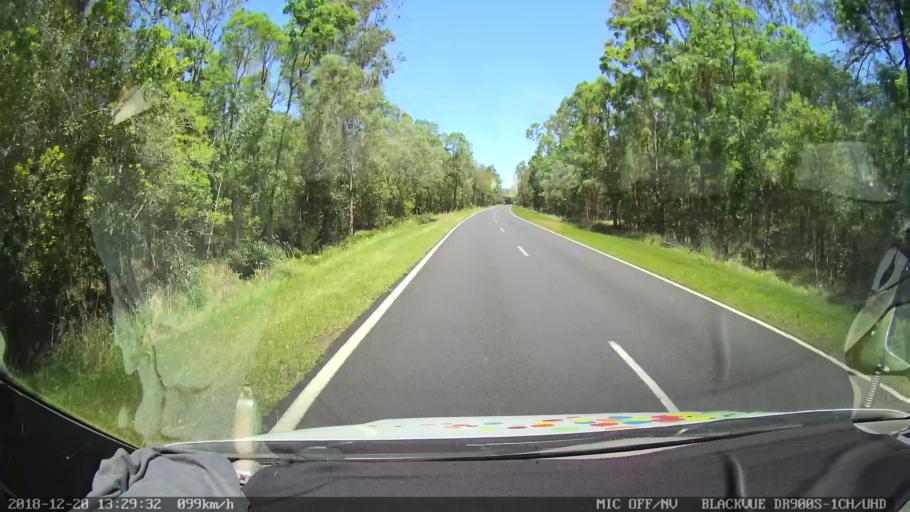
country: AU
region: New South Wales
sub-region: Clarence Valley
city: Gordon
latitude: -29.1905
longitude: 152.9901
